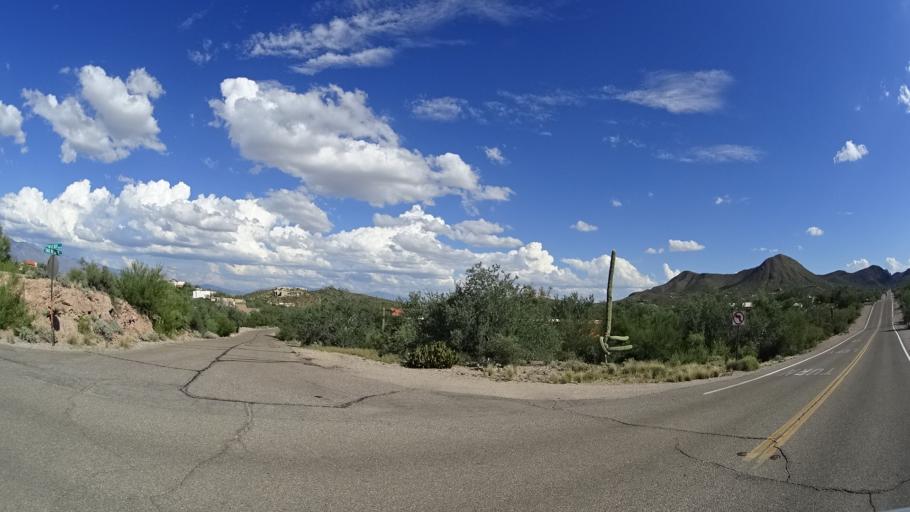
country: US
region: Arizona
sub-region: Pima County
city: Tucson Estates
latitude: 32.2451
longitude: -111.0628
